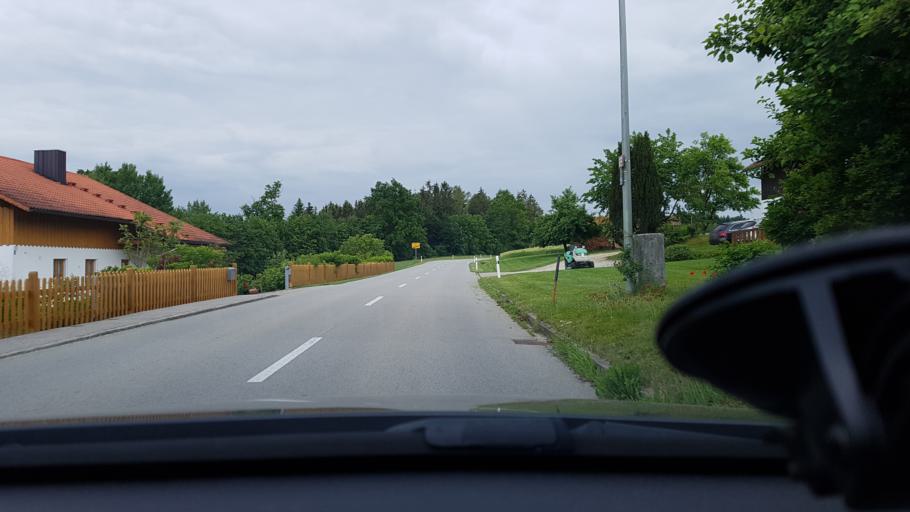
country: DE
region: Bavaria
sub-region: Lower Bavaria
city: Triftern
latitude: 48.3789
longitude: 13.0102
